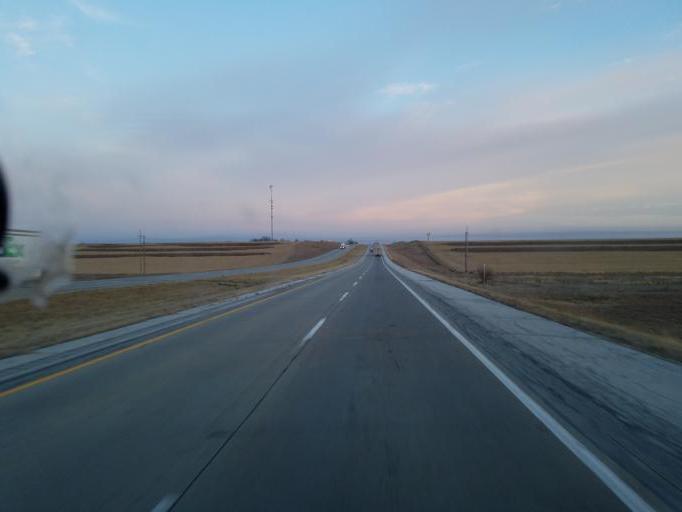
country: US
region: Iowa
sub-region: Pottawattamie County
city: Avoca
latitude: 41.4990
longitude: -95.4731
